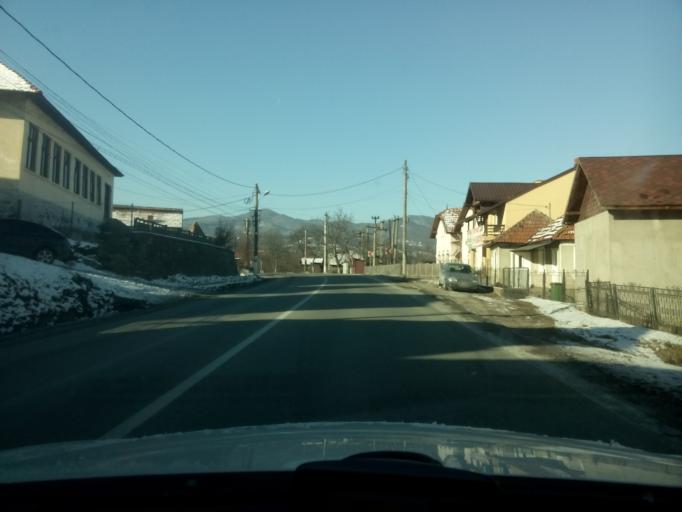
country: RO
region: Valcea
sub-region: Oras Calimanesti
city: Calimanesti
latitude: 45.2189
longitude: 24.3497
